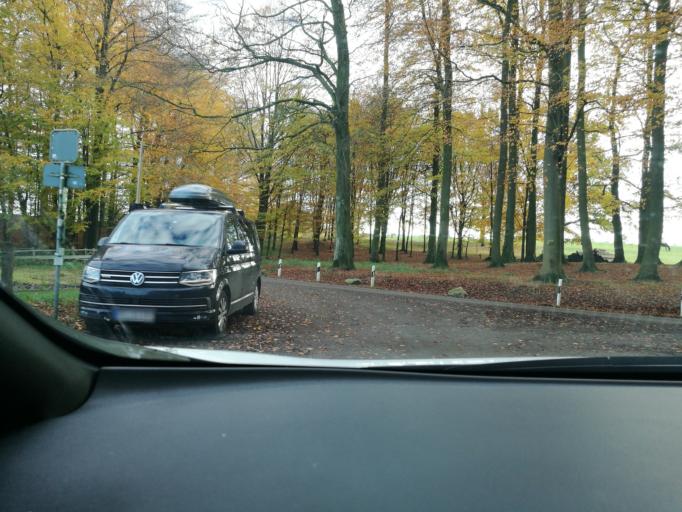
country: DE
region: Schleswig-Holstein
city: Holzbunge
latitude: 54.3845
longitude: 9.6983
